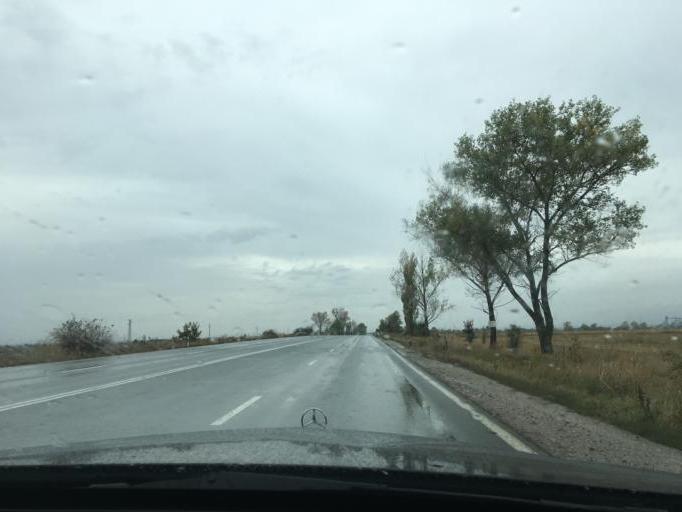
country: BG
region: Sofiya
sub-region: Obshtina Bozhurishte
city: Bozhurishte
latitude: 42.7893
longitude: 23.1557
